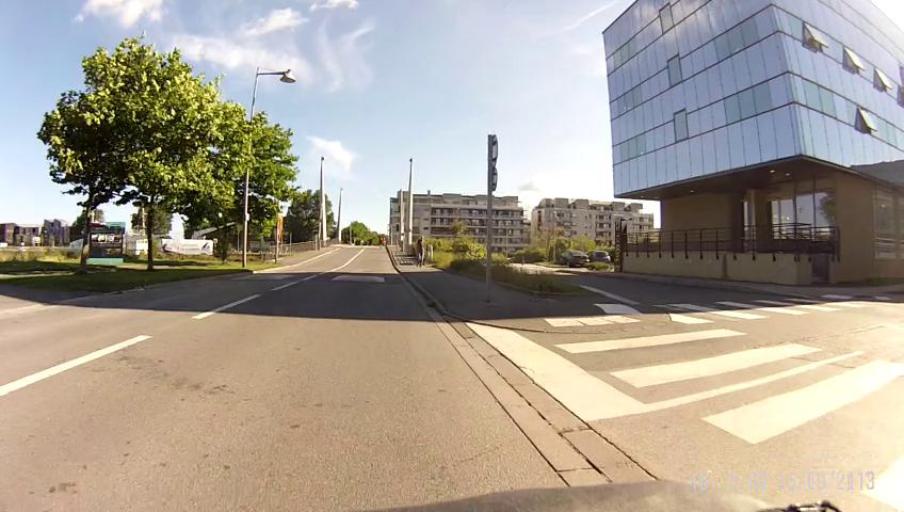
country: FR
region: Nord-Pas-de-Calais
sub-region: Departement du Nord
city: Dunkerque
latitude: 51.0417
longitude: 2.3750
